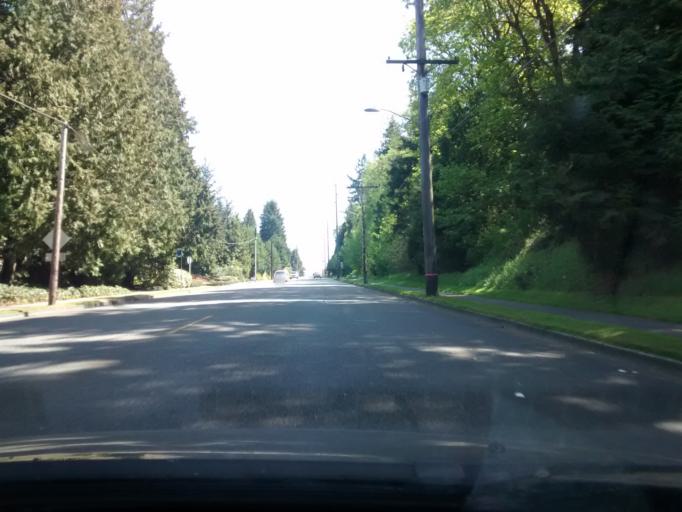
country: US
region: Washington
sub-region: Snohomish County
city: Edmonds
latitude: 47.8105
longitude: -122.3604
